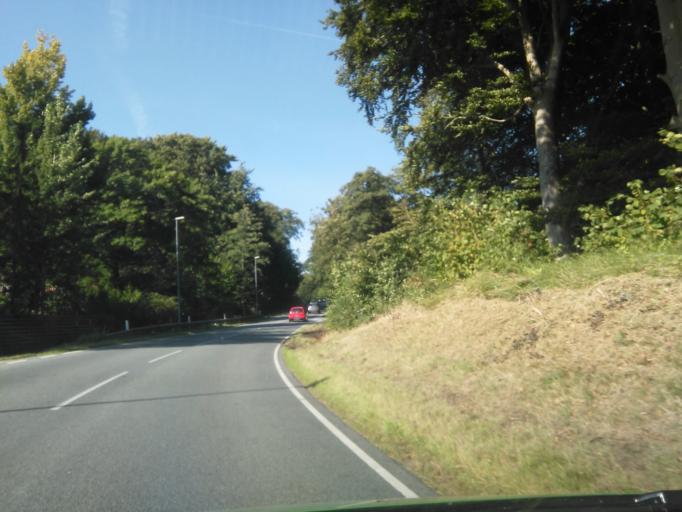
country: DK
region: Central Jutland
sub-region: Syddjurs Kommune
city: Ebeltoft
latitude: 56.2358
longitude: 10.5841
